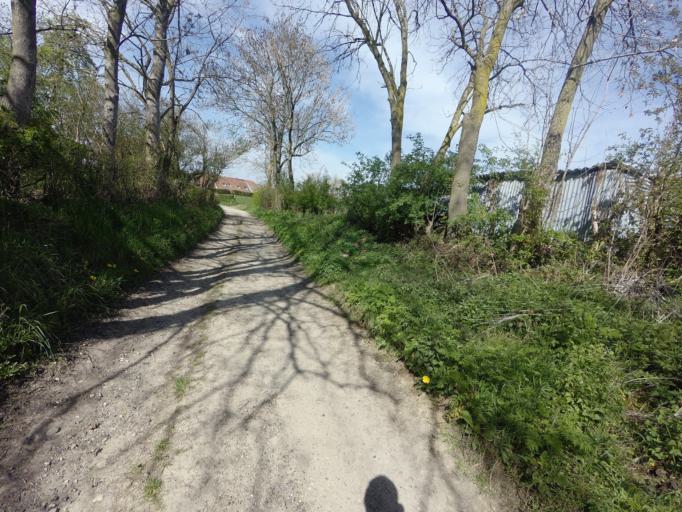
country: NL
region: Limburg
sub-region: Eijsden-Margraten
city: Margraten
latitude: 50.7860
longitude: 5.8167
